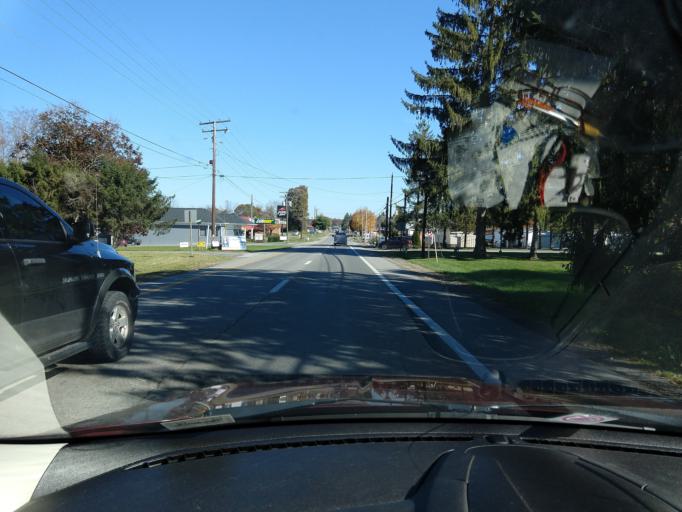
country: US
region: West Virginia
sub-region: Greenbrier County
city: Fairlea
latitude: 37.7726
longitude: -80.4624
